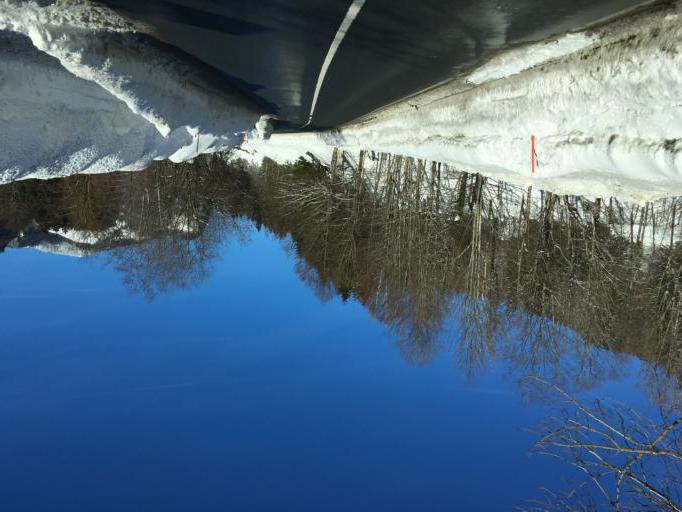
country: AT
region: Tyrol
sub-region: Politischer Bezirk Kufstein
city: Rettenschoss
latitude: 47.7192
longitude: 12.2891
